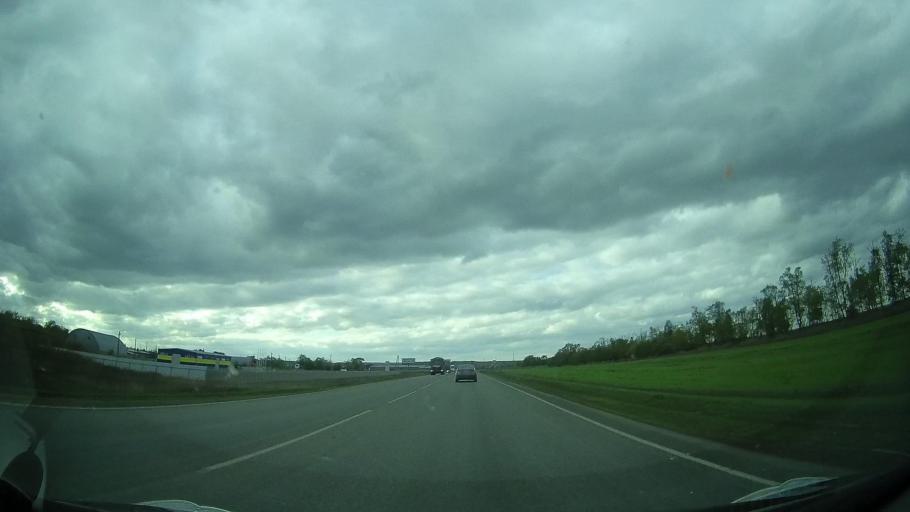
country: RU
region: Rostov
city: Kagal'nitskaya
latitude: 46.8723
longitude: 40.1651
